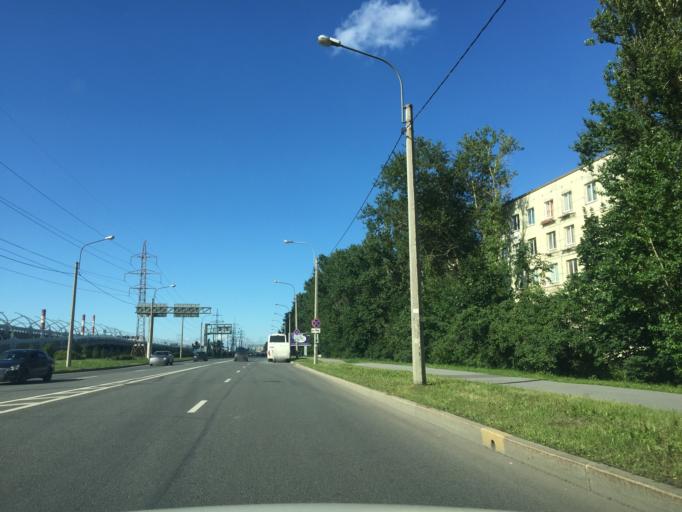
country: RU
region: St.-Petersburg
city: Avtovo
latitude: 59.8530
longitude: 30.2930
